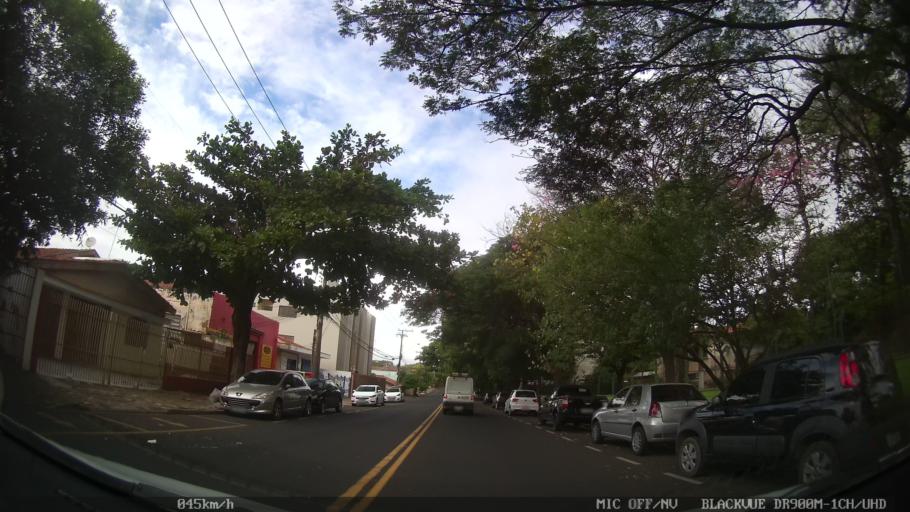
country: BR
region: Sao Paulo
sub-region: Sao Jose Do Rio Preto
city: Sao Jose do Rio Preto
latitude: -20.8231
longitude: -49.3701
